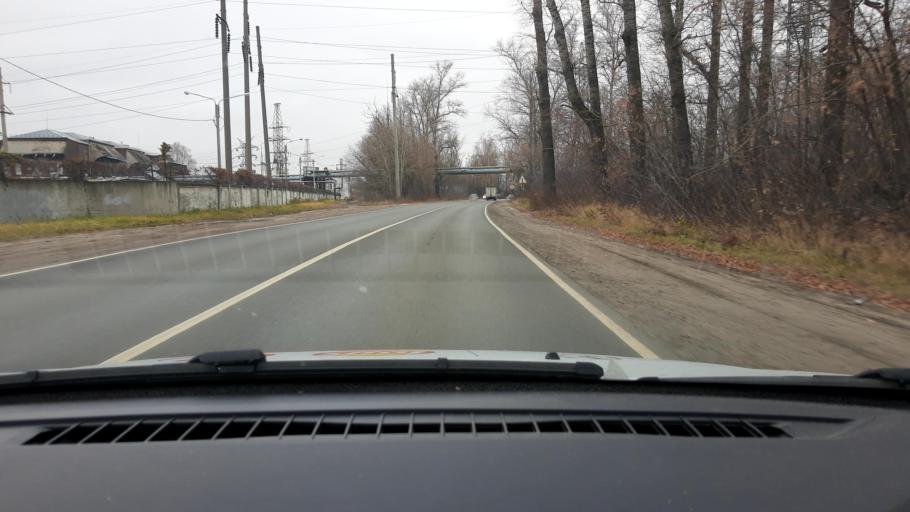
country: RU
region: Nizjnij Novgorod
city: Novaya Balakhna
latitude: 56.5015
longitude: 43.5931
